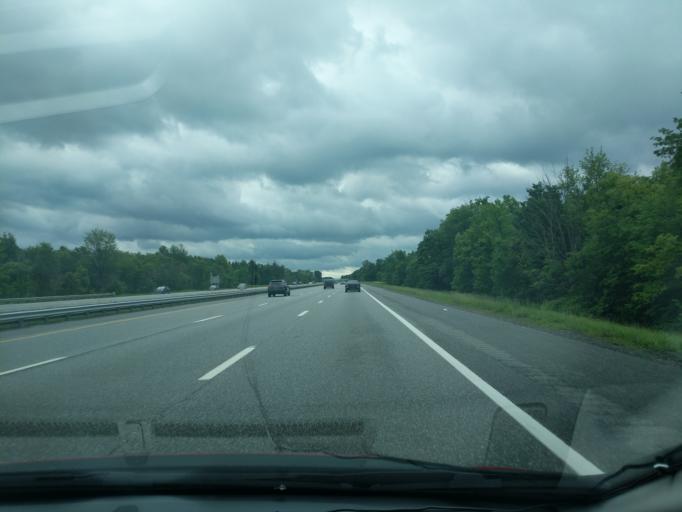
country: US
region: Ohio
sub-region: Cuyahoga County
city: Strongsville
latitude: 41.2878
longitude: -81.8084
